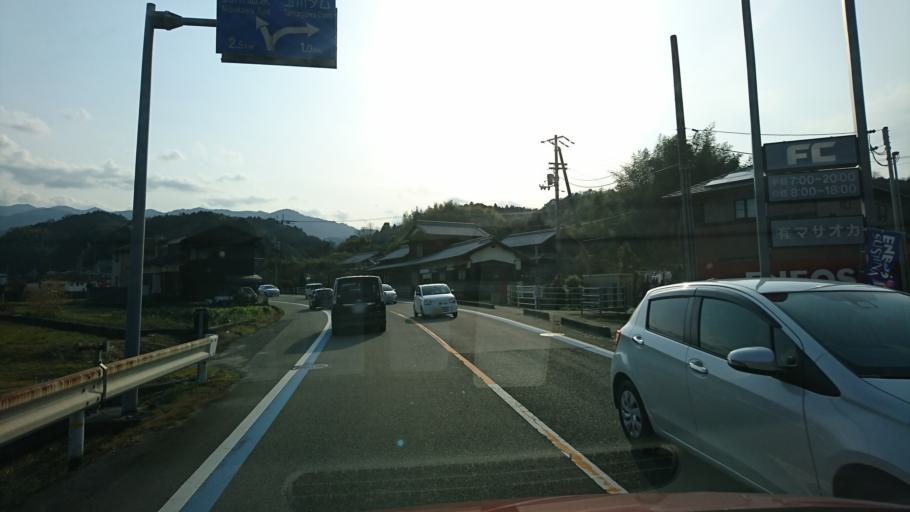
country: JP
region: Ehime
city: Hojo
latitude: 34.0038
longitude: 132.9382
